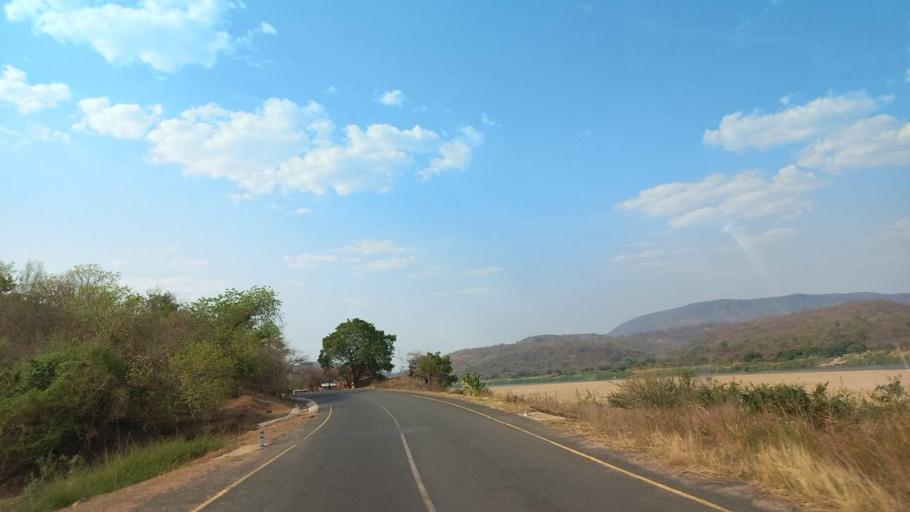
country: ZM
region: Lusaka
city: Luangwa
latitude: -14.9986
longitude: 30.2146
